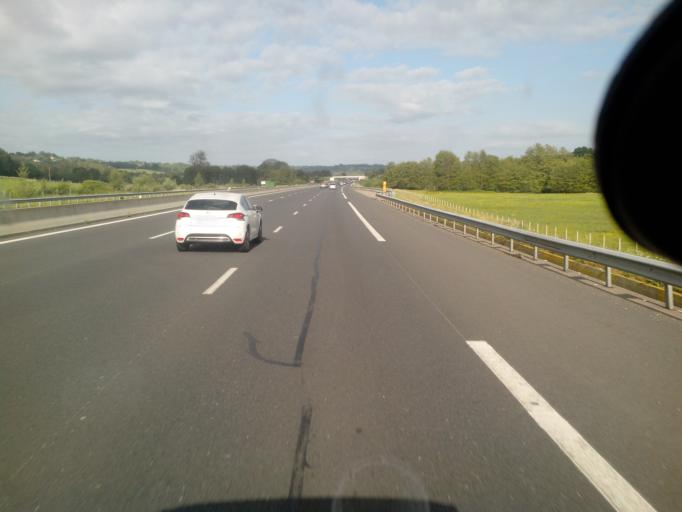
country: FR
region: Lower Normandy
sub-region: Departement du Calvados
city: Saint-Gatien-des-Bois
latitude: 49.2994
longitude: 0.2322
